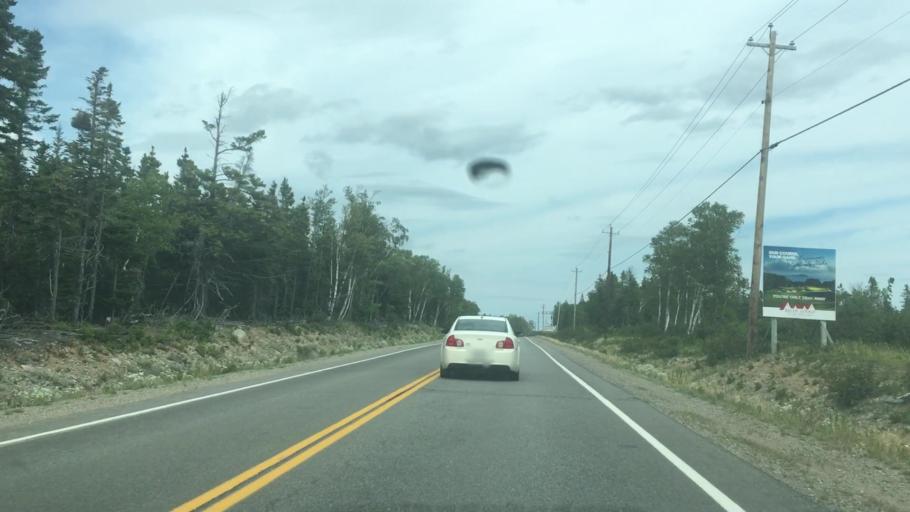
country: CA
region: Nova Scotia
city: Sydney Mines
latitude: 46.5183
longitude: -60.4244
